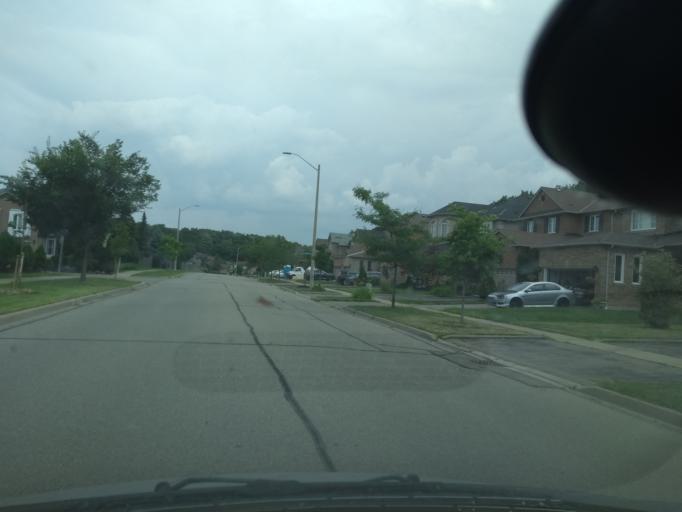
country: CA
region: Ontario
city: Mississauga
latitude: 43.6211
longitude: -79.6573
